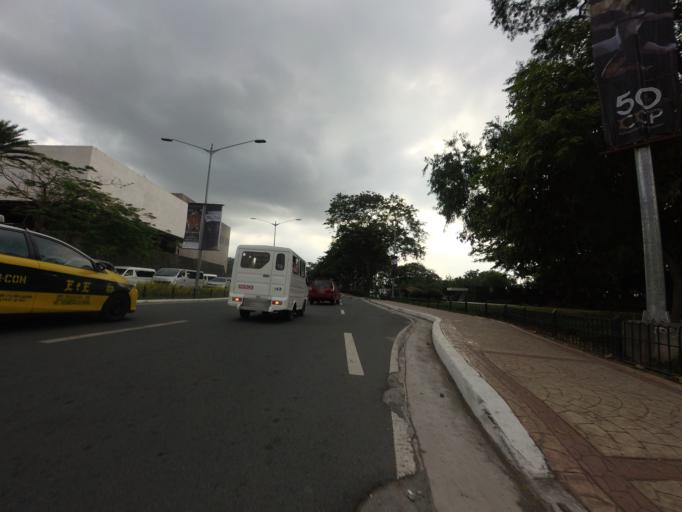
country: PH
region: Metro Manila
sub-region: City of Manila
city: Port Area
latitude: 14.5592
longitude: 120.9861
